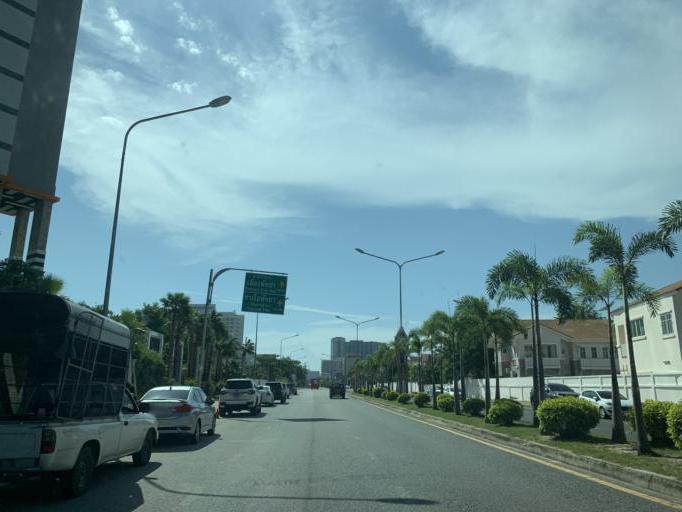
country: TH
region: Chon Buri
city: Phatthaya
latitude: 12.8833
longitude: 100.8858
